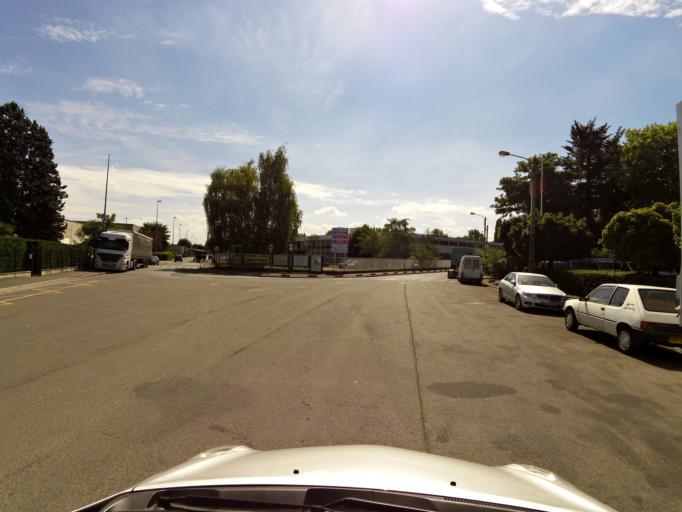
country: FR
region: Ile-de-France
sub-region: Departement de Seine-et-Marne
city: Chelles
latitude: 48.8705
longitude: 2.5954
